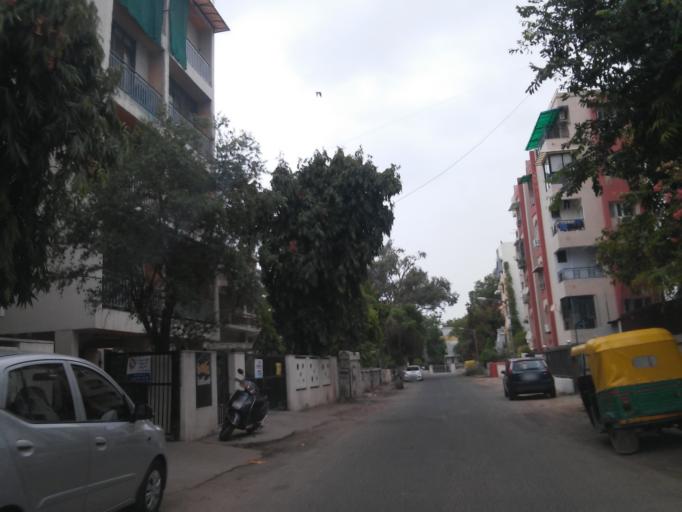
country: IN
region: Gujarat
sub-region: Ahmadabad
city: Ahmedabad
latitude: 23.0123
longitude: 72.5607
